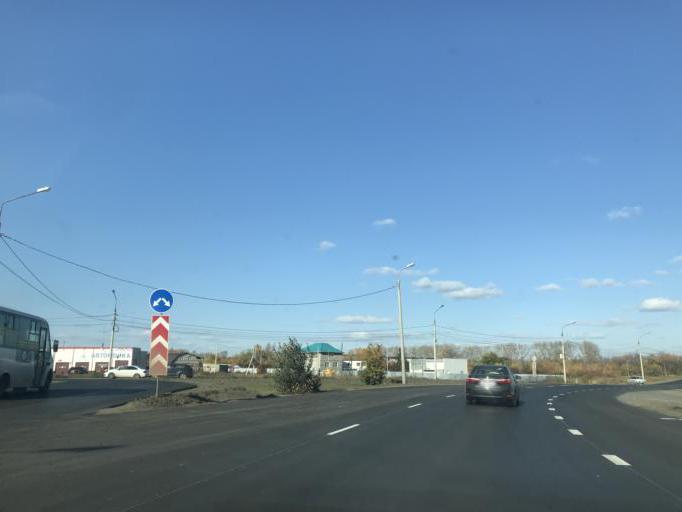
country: RU
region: Chelyabinsk
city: Roshchino
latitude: 55.2303
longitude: 61.2874
